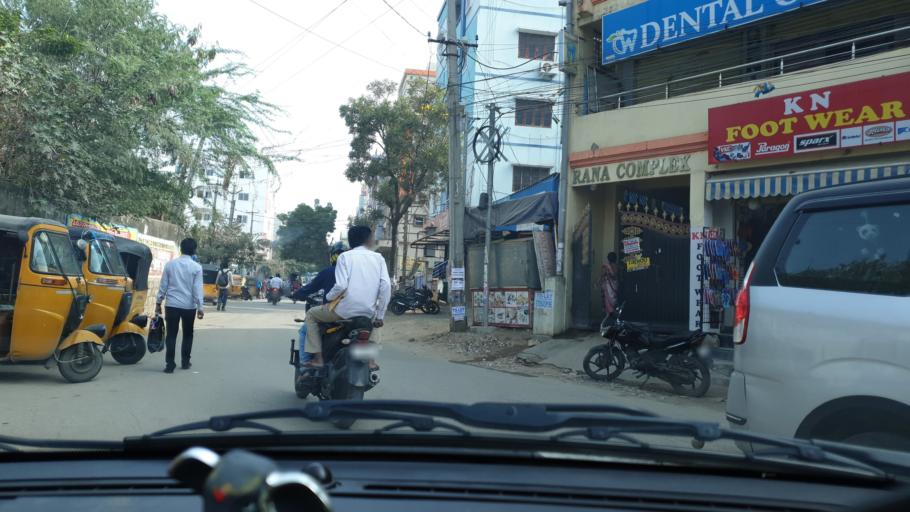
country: IN
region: Telangana
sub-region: Rangareddi
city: Kukatpalli
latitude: 17.4841
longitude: 78.4087
